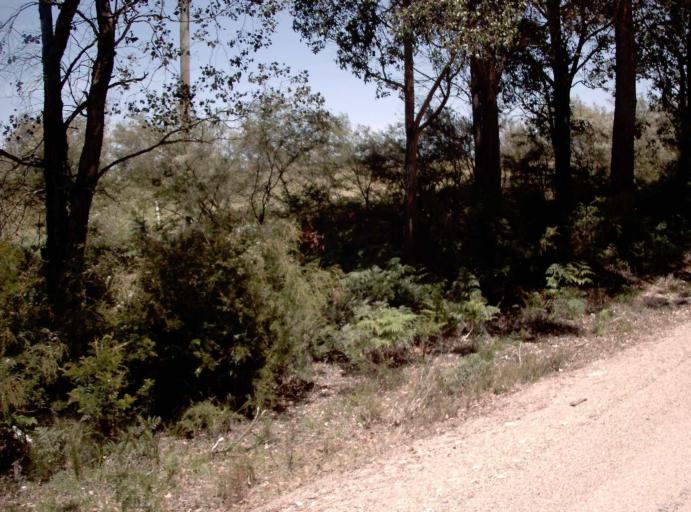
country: AU
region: Victoria
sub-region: East Gippsland
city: Bairnsdale
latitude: -37.7320
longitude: 147.7852
